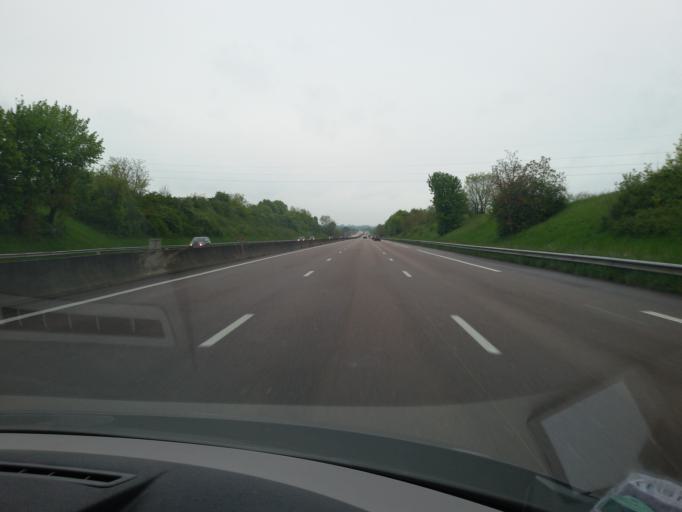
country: FR
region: Rhone-Alpes
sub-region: Departement de l'Ain
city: Pont-de-Vaux
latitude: 46.4679
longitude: 4.8812
